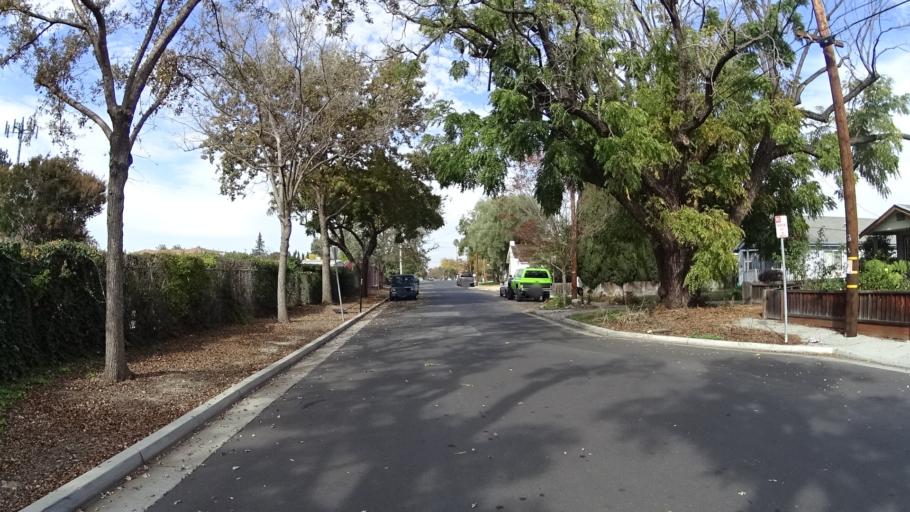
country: US
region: California
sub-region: Santa Clara County
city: Santa Clara
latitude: 37.3413
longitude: -121.9470
